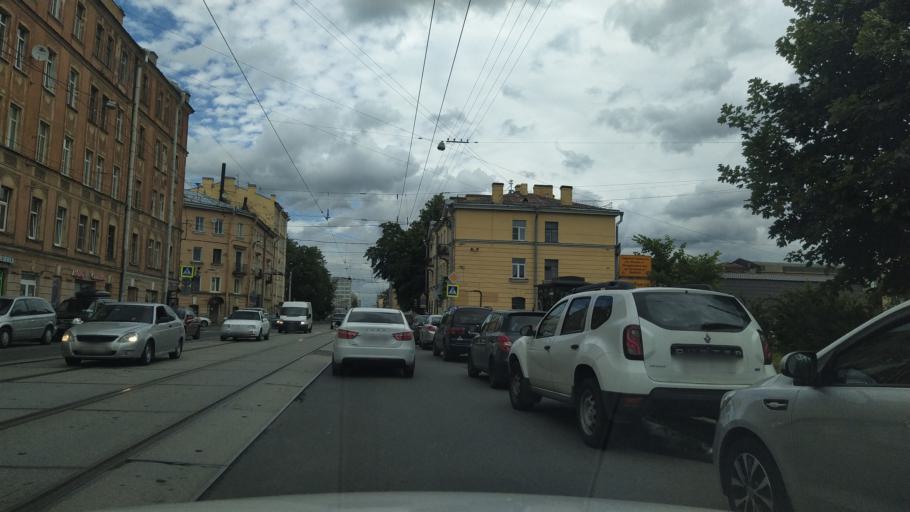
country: RU
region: Leningrad
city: Finlyandskiy
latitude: 59.9656
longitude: 30.3822
